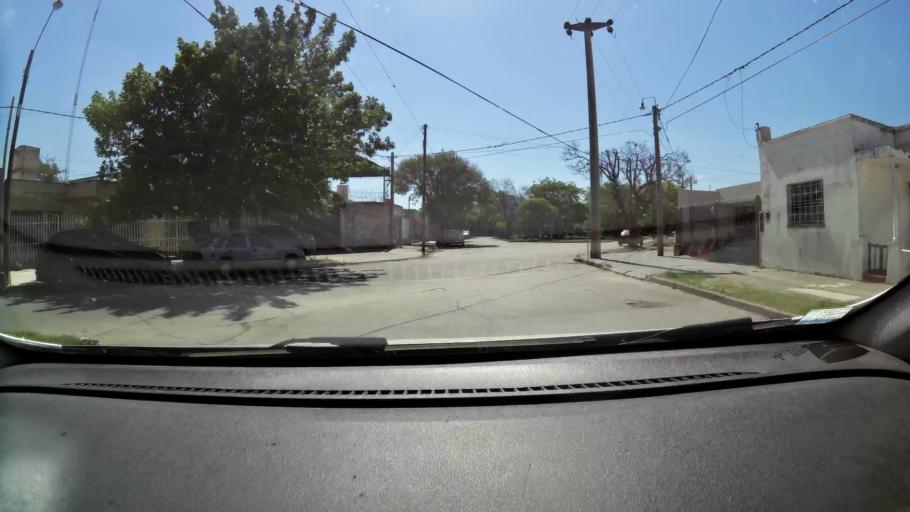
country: AR
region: Cordoba
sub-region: Departamento de Capital
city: Cordoba
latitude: -31.3770
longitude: -64.1540
